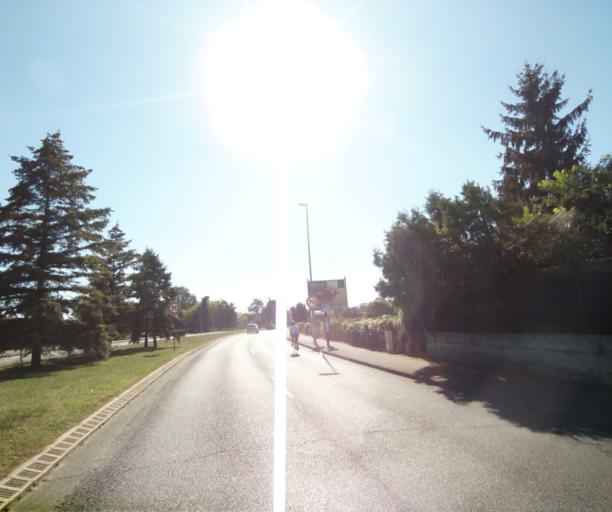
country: FR
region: Auvergne
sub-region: Departement du Puy-de-Dome
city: Gerzat
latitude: 45.7955
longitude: 3.1231
